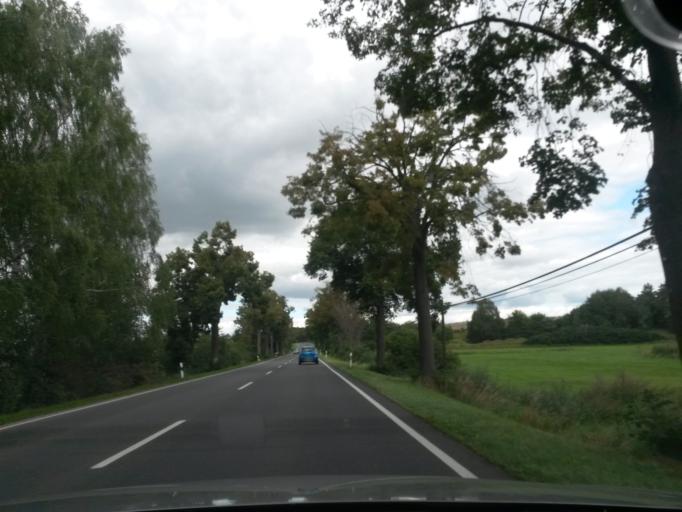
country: DE
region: Brandenburg
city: Angermunde
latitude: 52.9944
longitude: 13.9837
